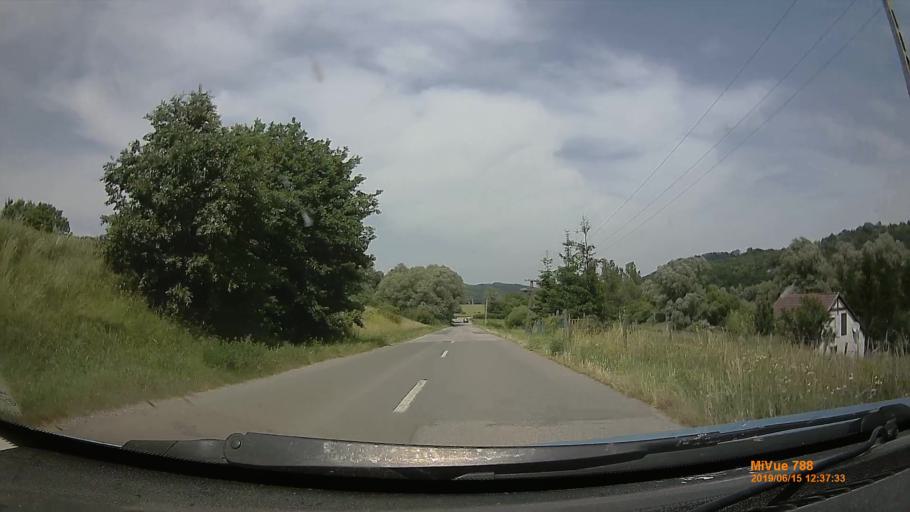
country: HU
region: Baranya
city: Sasd
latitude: 46.1744
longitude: 18.0874
